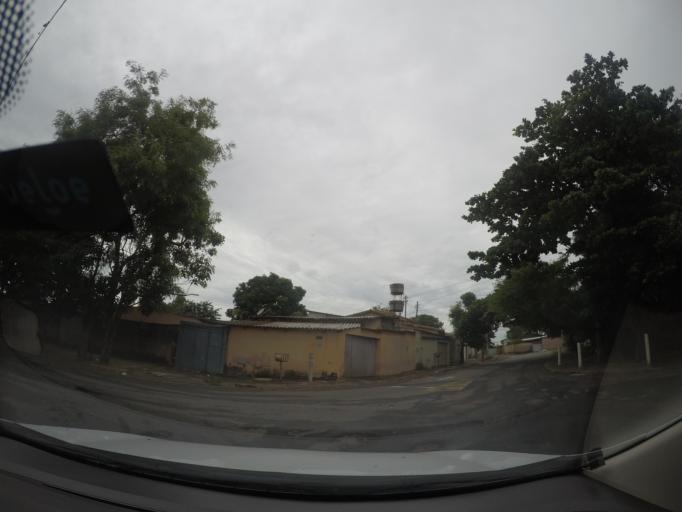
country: BR
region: Goias
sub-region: Goiania
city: Goiania
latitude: -16.6763
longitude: -49.2353
